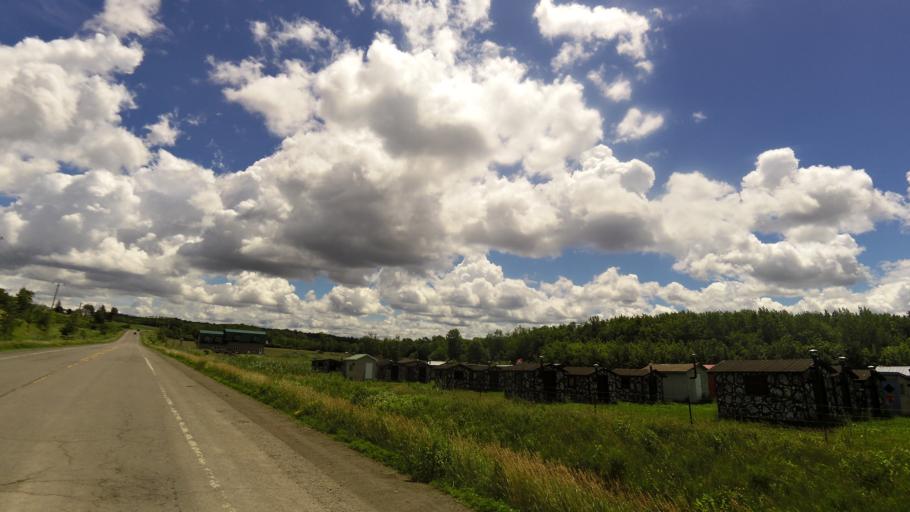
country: CA
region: Quebec
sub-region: Monteregie
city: Rigaud
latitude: 45.5371
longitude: -74.3187
